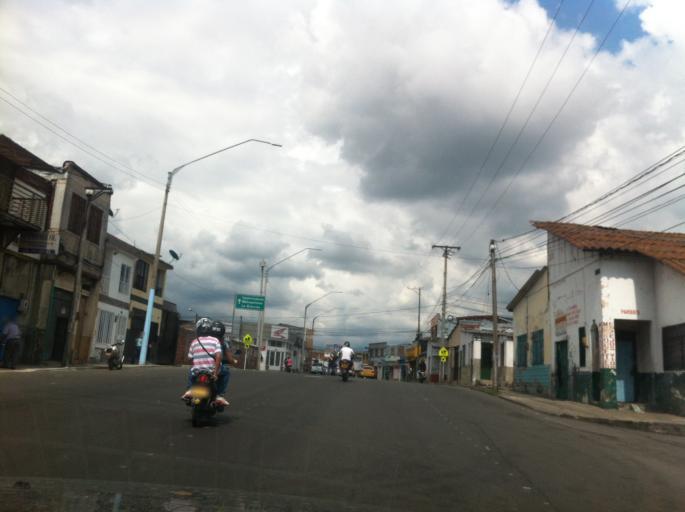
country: CO
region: Quindio
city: Armenia
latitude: 4.5293
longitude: -75.6810
